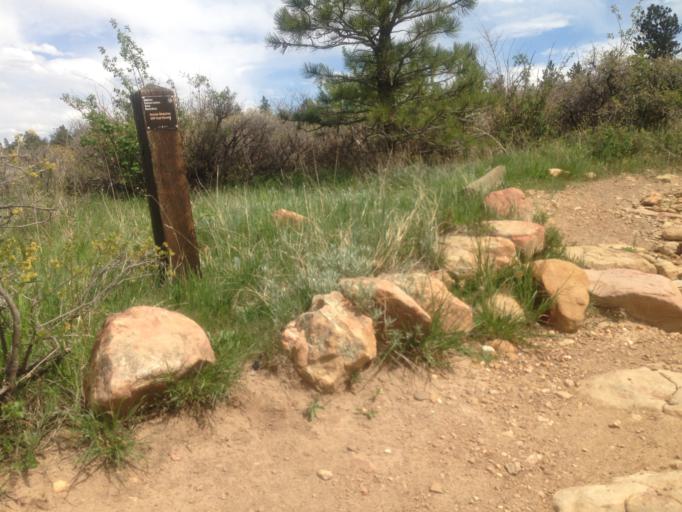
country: US
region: Colorado
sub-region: Boulder County
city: Superior
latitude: 39.9479
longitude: -105.2295
